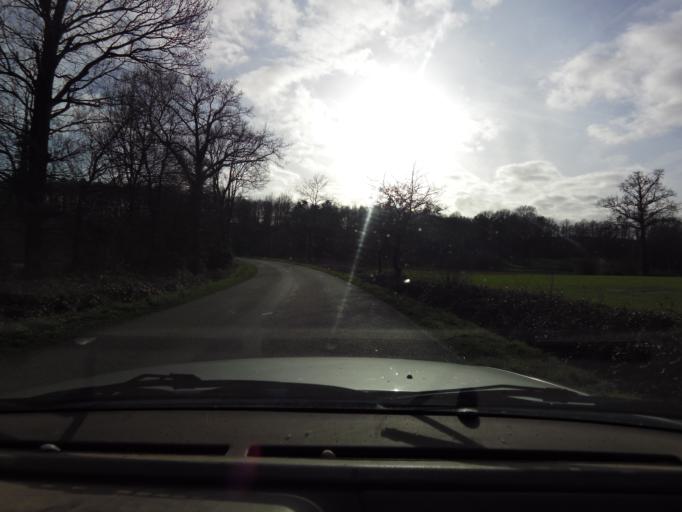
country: FR
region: Brittany
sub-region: Departement du Morbihan
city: Limerzel
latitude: 47.6539
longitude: -2.3603
